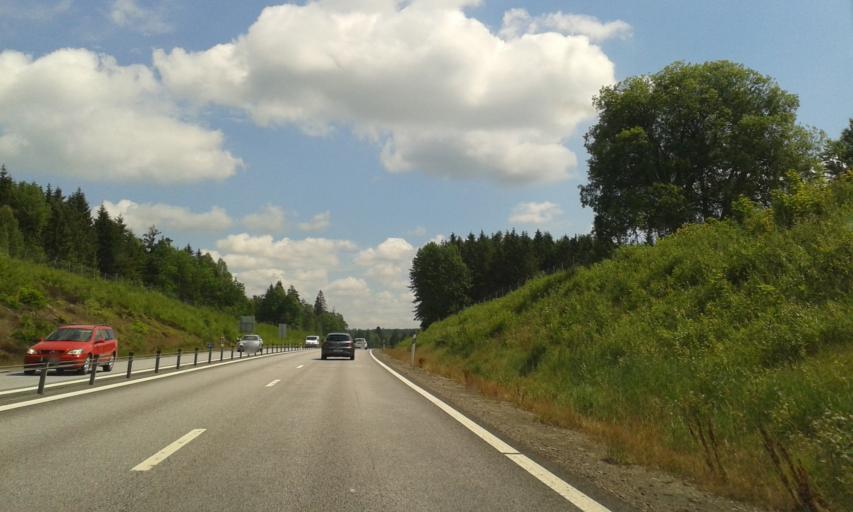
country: SE
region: Kronoberg
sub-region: Alvesta Kommun
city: Alvesta
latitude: 56.9206
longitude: 14.5996
